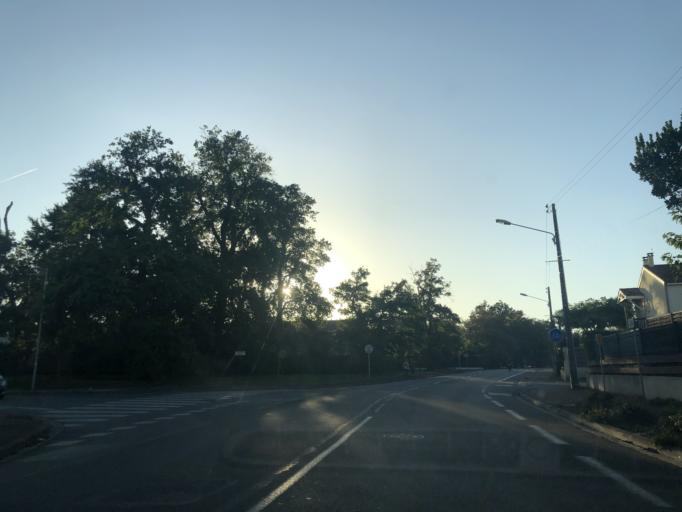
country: FR
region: Aquitaine
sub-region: Departement de la Gironde
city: Merignac
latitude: 44.8464
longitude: -0.6348
